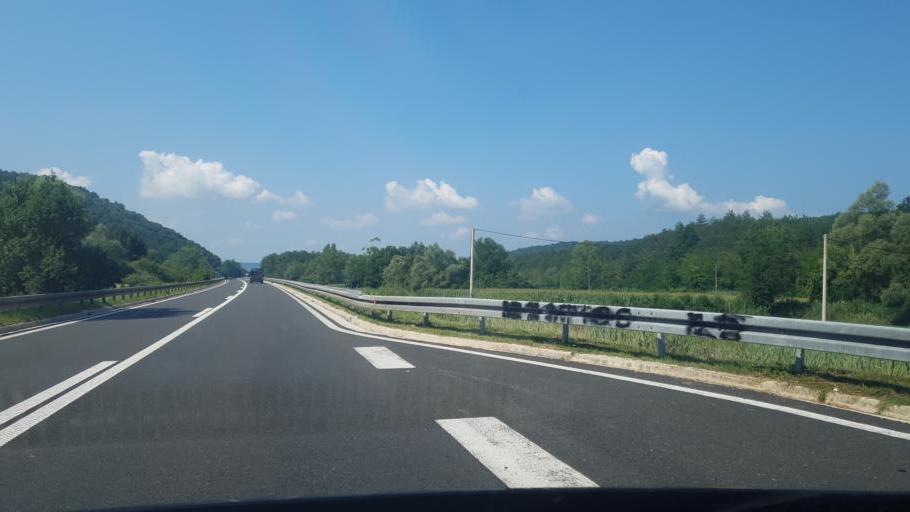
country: HR
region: Istarska
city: Pazin
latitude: 45.2883
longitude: 14.0322
